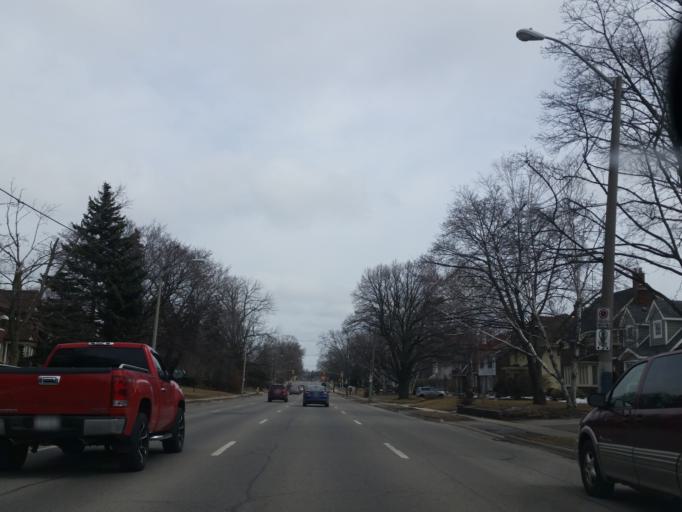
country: CA
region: Ontario
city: Oshawa
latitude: 43.9005
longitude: -78.8510
